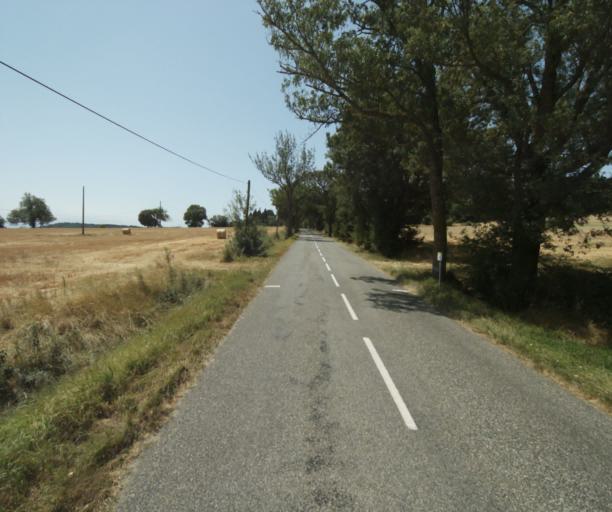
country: FR
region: Midi-Pyrenees
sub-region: Departement de la Haute-Garonne
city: Saint-Felix-Lauragais
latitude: 43.4322
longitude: 1.8926
